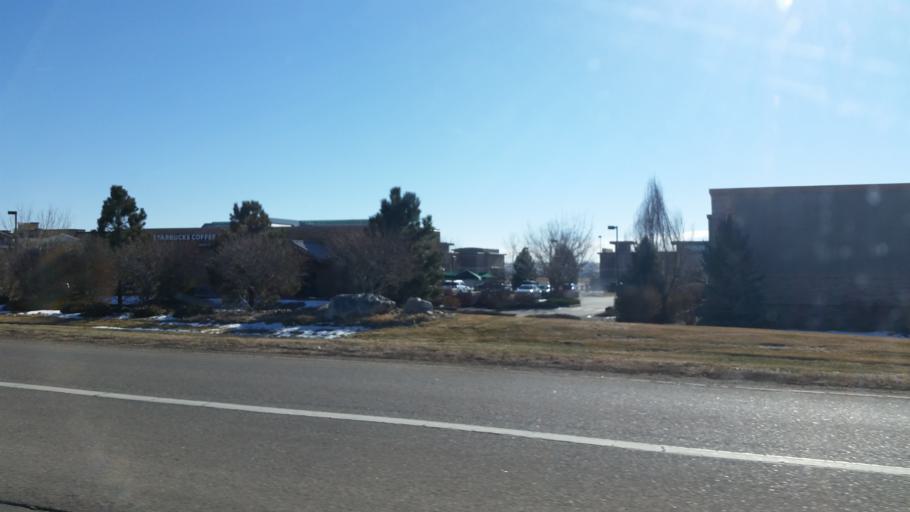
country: US
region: Colorado
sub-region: Larimer County
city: Loveland
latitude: 40.4071
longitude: -104.9819
